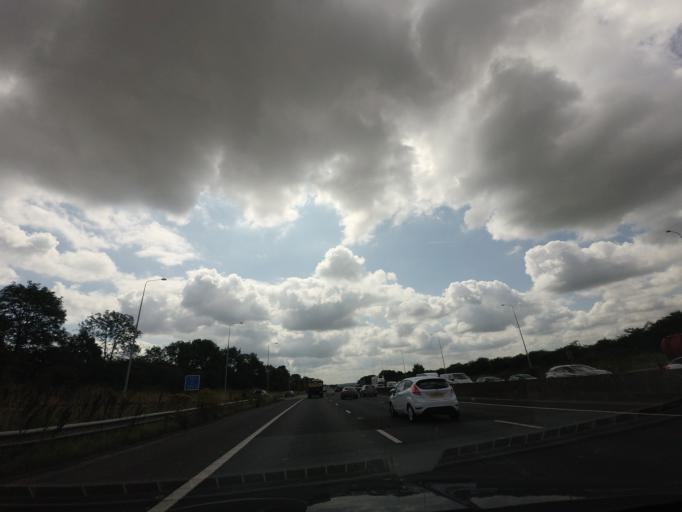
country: GB
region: England
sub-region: Borough of Wigan
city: Shevington
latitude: 53.5872
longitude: -2.6937
